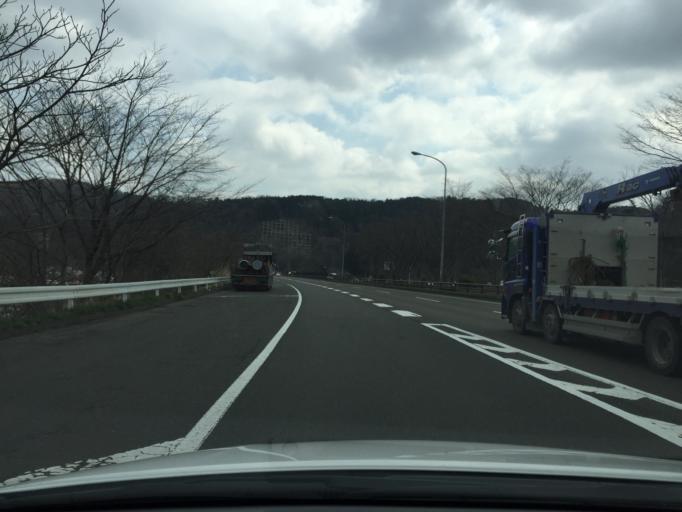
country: JP
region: Miyagi
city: Sendai
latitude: 38.2598
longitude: 140.8183
